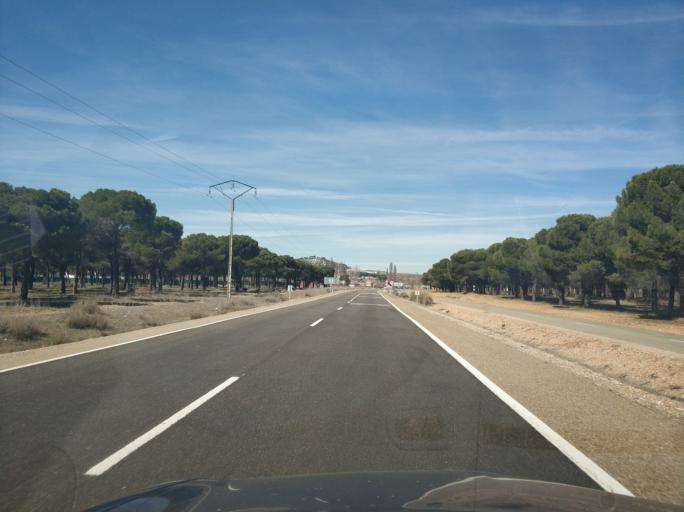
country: ES
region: Castille and Leon
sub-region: Provincia de Valladolid
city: Simancas
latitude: 41.5786
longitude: -4.8128
